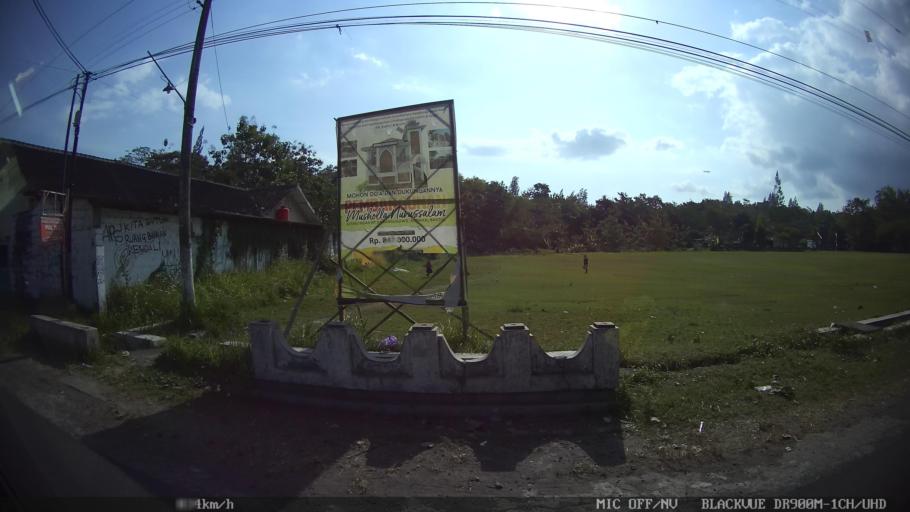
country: ID
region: Daerah Istimewa Yogyakarta
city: Kasihan
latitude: -7.8371
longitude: 110.3364
